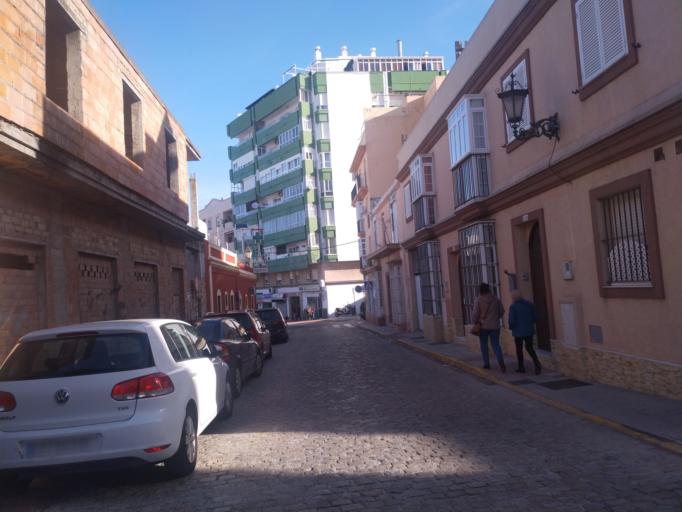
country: ES
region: Andalusia
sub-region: Provincia de Cadiz
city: San Fernando
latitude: 36.4733
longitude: -6.1950
